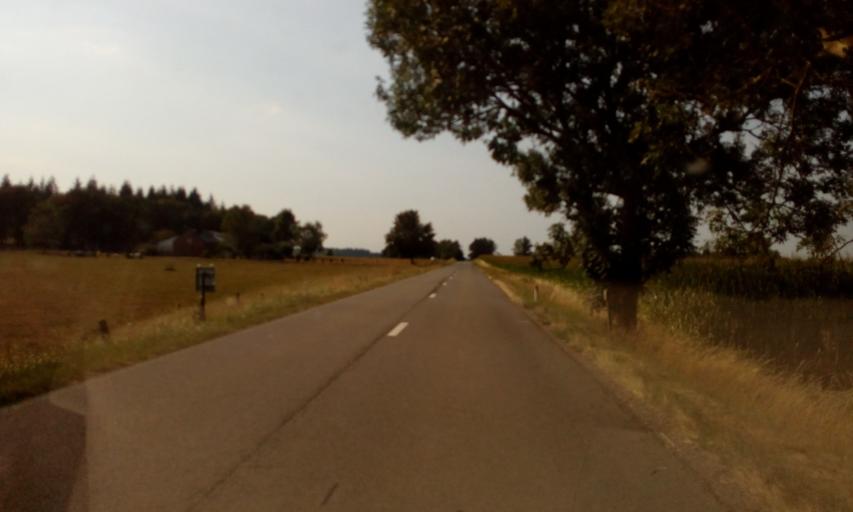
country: BE
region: Wallonia
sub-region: Province de Namur
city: Rochefort
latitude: 50.1345
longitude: 5.2306
